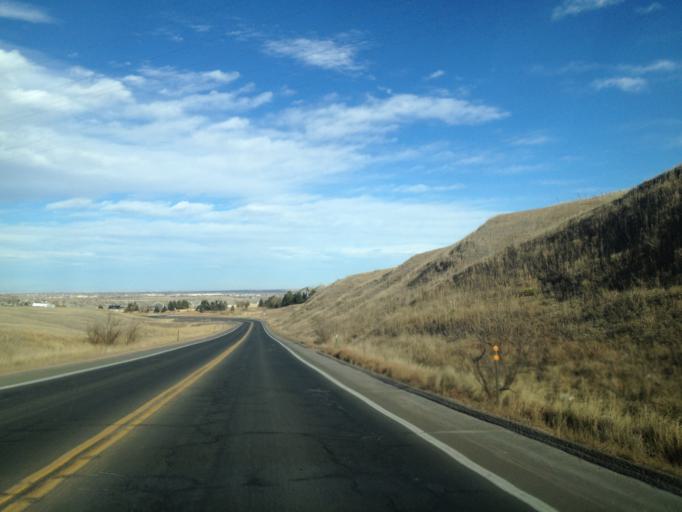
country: US
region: Colorado
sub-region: Boulder County
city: Superior
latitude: 39.9133
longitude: -105.1670
